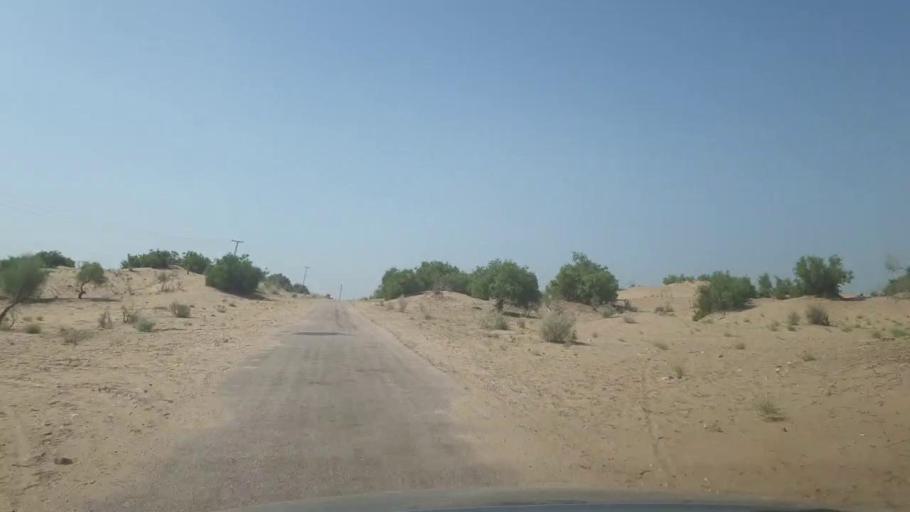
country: PK
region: Sindh
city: Rohri
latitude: 27.4255
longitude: 69.0791
